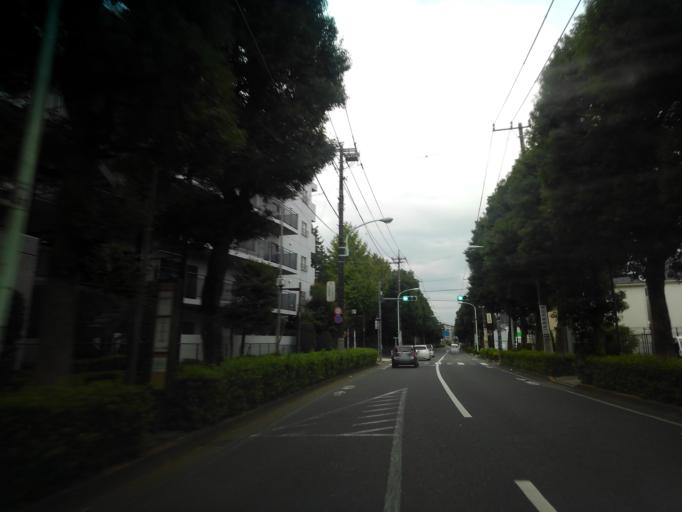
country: JP
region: Tokyo
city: Chofugaoka
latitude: 35.6592
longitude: 139.5406
